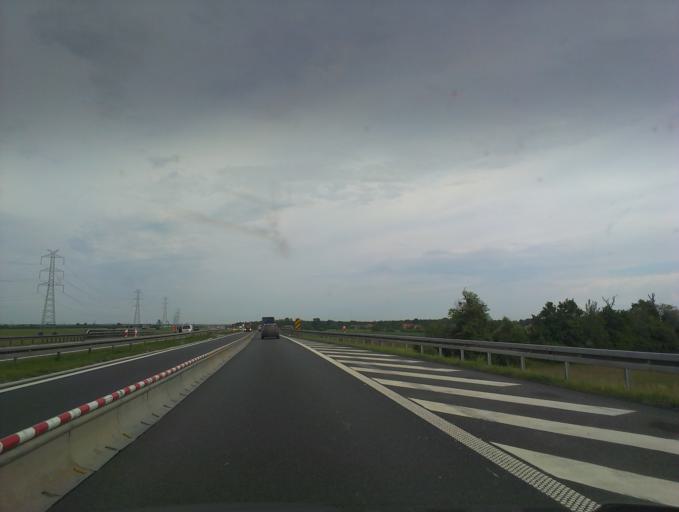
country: PL
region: Opole Voivodeship
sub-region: Powiat brzeski
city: Losiow
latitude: 50.7241
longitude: 17.5230
